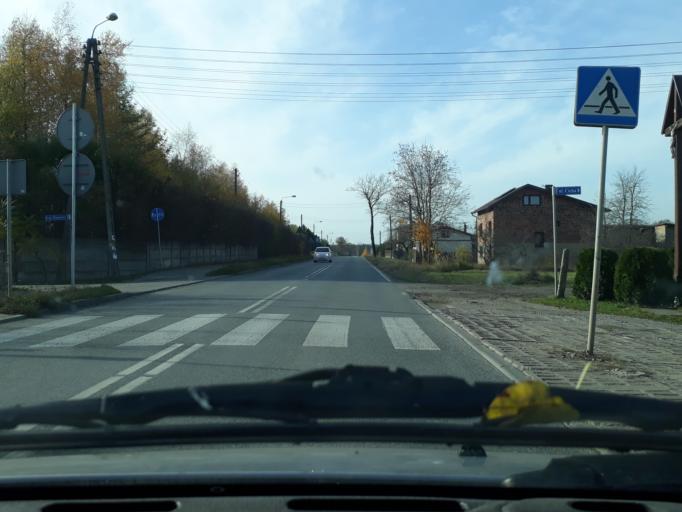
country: PL
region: Silesian Voivodeship
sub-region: Powiat lubliniecki
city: Psary
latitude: 50.5768
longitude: 18.9926
